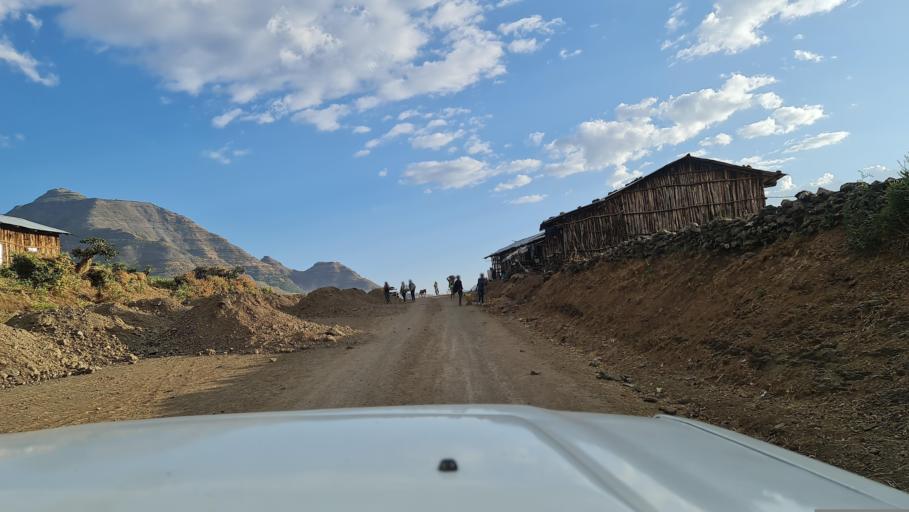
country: ET
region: Amhara
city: Debark'
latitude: 13.0393
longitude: 38.0384
